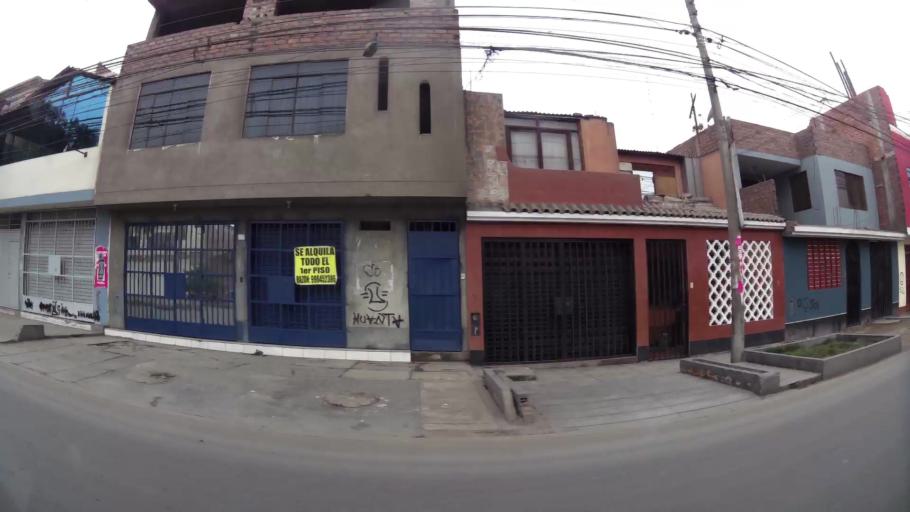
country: PE
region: Lima
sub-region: Lima
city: Independencia
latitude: -11.9871
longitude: -76.9958
